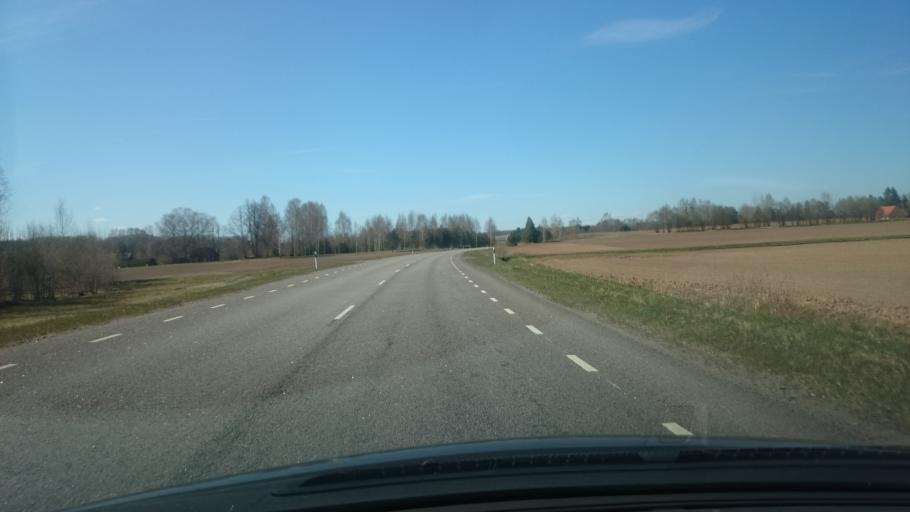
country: EE
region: Polvamaa
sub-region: Polva linn
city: Polva
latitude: 58.2456
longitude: 27.0049
